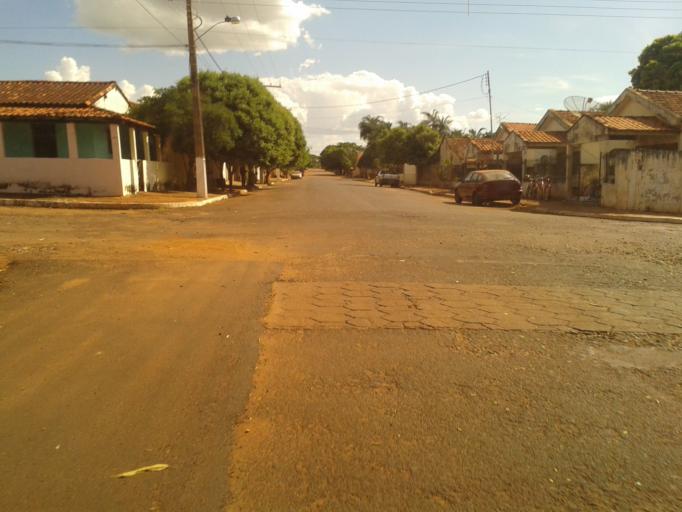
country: BR
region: Minas Gerais
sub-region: Santa Vitoria
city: Santa Vitoria
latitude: -18.6947
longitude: -49.9427
